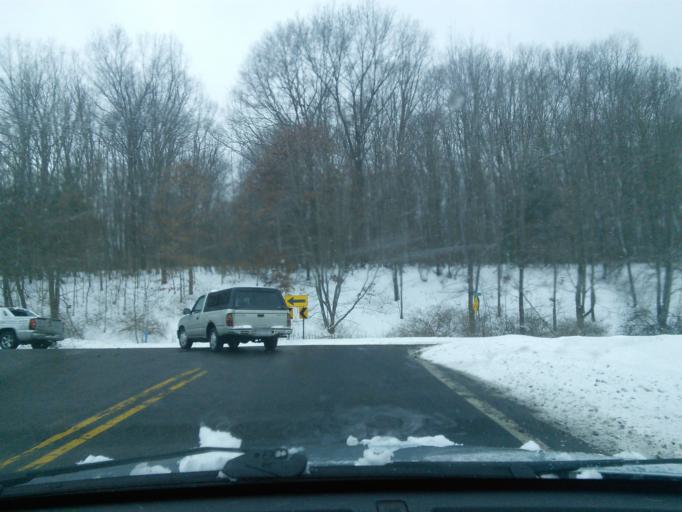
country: US
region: Pennsylvania
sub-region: Centre County
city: Park Forest Village
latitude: 40.8217
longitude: -77.9015
